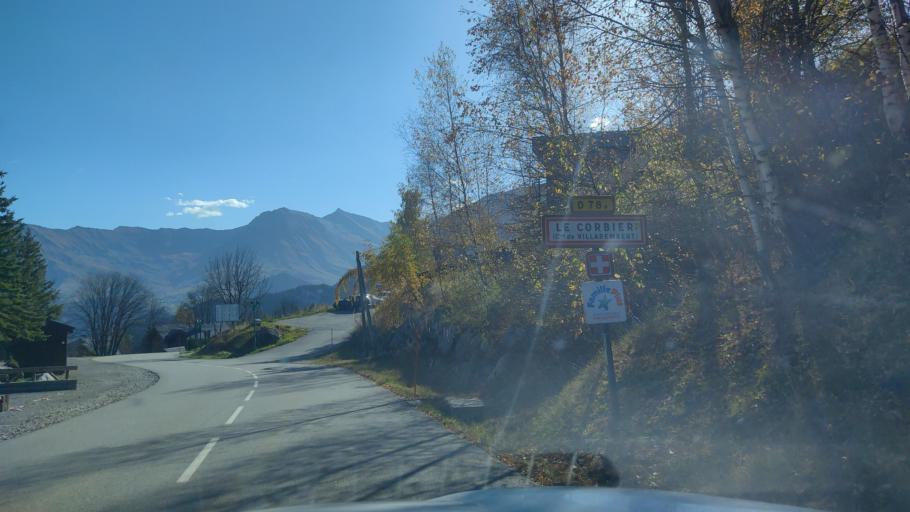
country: FR
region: Rhone-Alpes
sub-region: Departement de la Savoie
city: Saint-Jean-de-Maurienne
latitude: 45.2444
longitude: 6.2641
